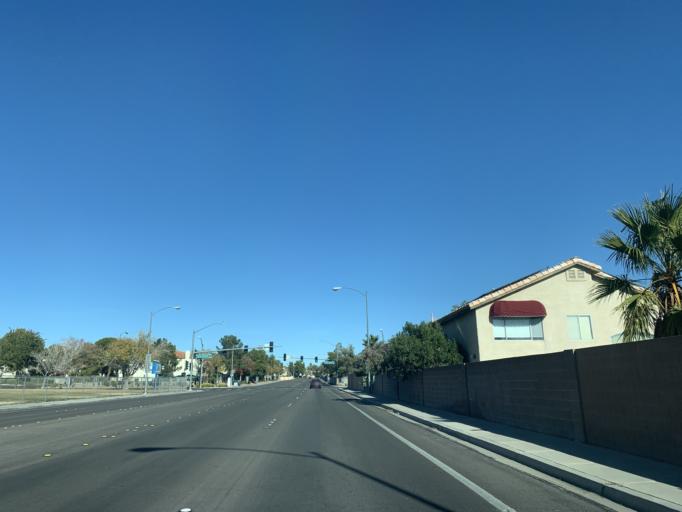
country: US
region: Nevada
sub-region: Clark County
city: Summerlin South
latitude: 36.1250
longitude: -115.2879
